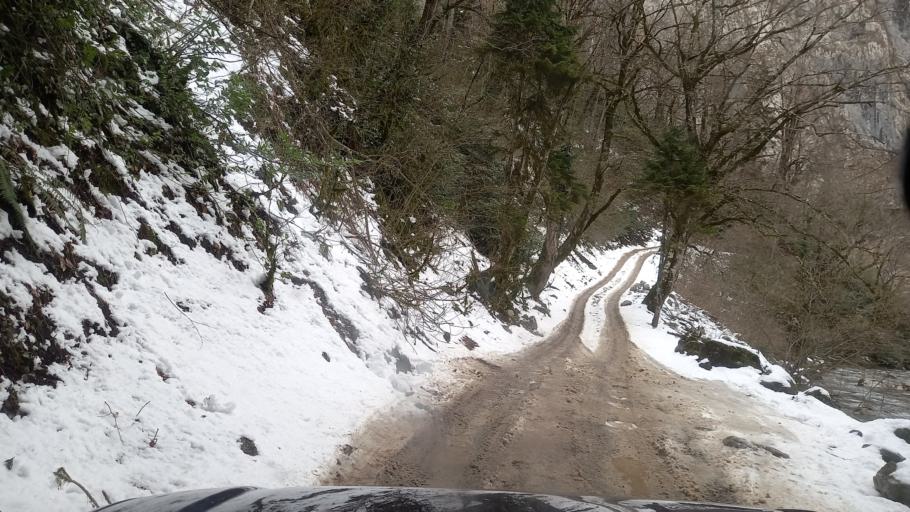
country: GE
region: Abkhazia
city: Gagra
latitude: 43.4335
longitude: 40.4439
